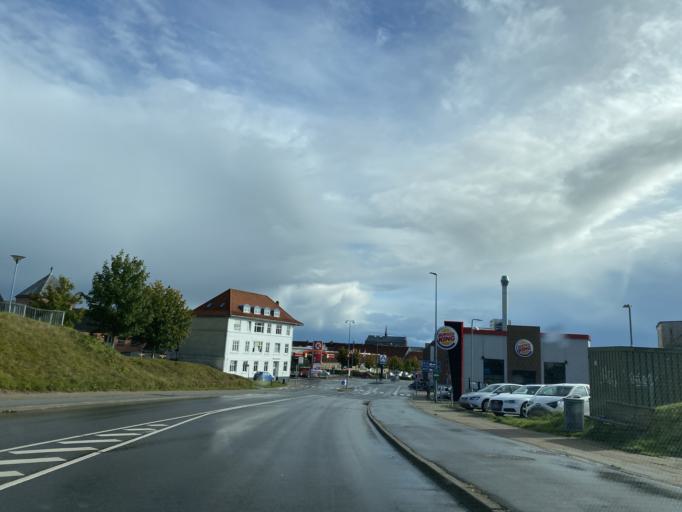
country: DK
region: South Denmark
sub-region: Haderslev Kommune
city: Haderslev
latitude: 55.2547
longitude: 9.4821
